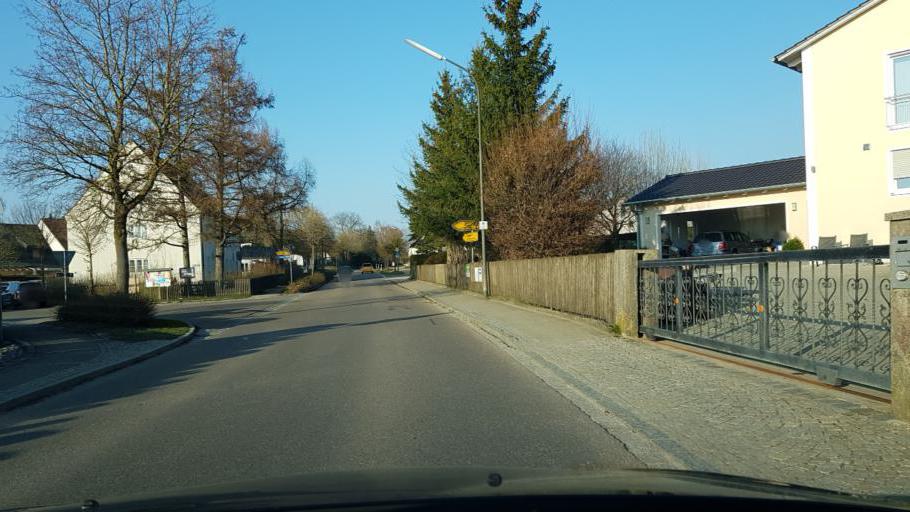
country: DE
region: Bavaria
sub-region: Upper Bavaria
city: Altomunster
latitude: 48.3923
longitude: 11.2608
